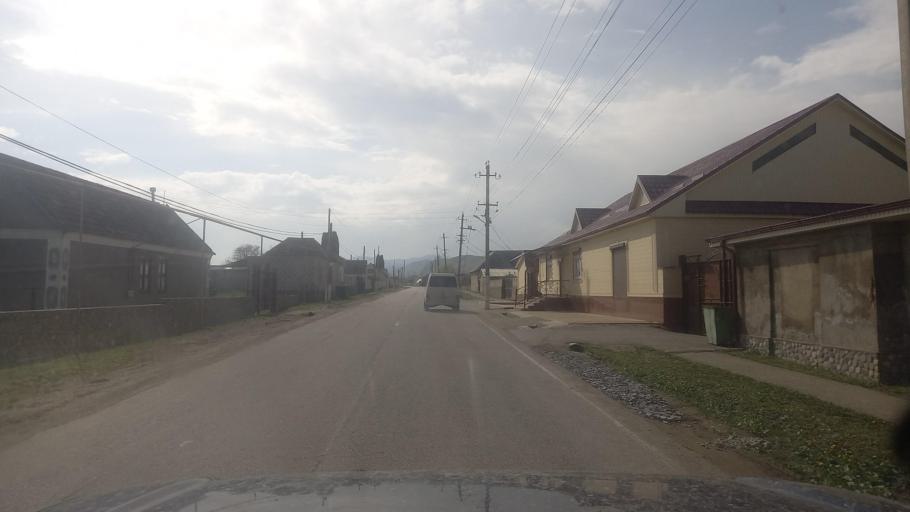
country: RU
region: Kabardino-Balkariya
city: Kamennomostskoye
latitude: 43.7343
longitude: 43.0441
